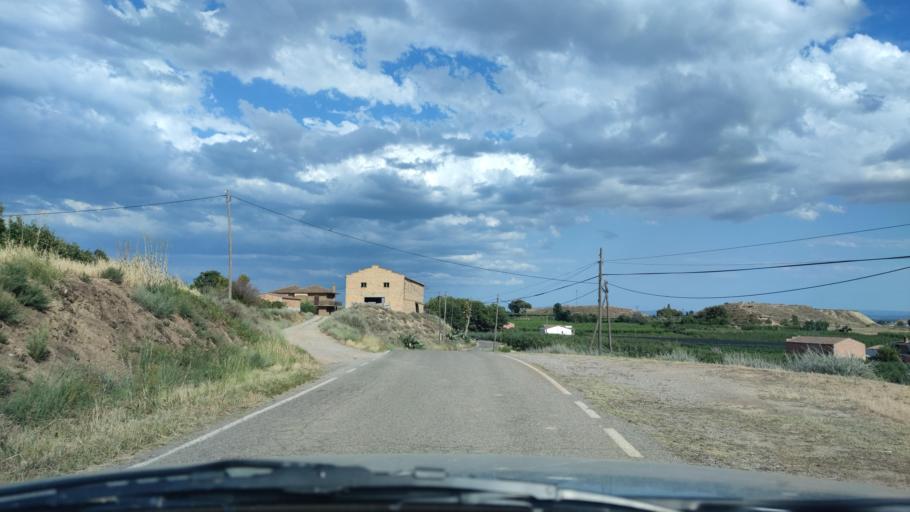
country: ES
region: Catalonia
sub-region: Provincia de Lleida
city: Alpicat
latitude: 41.6298
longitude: 0.5677
